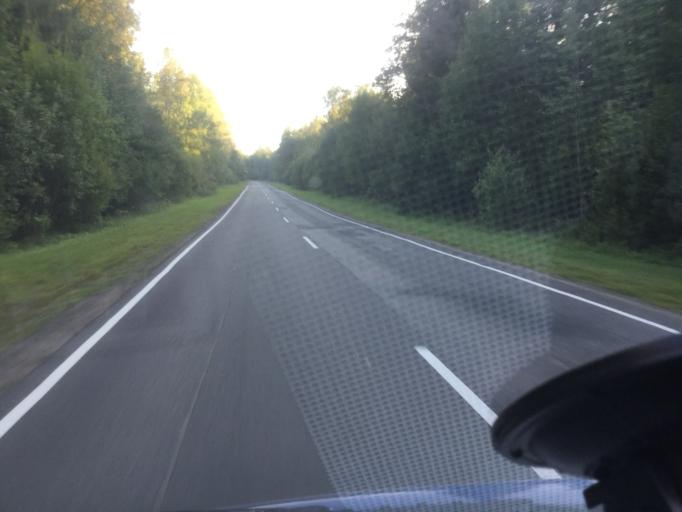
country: BY
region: Vitebsk
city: Navapolatsk
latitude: 55.7290
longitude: 28.5858
